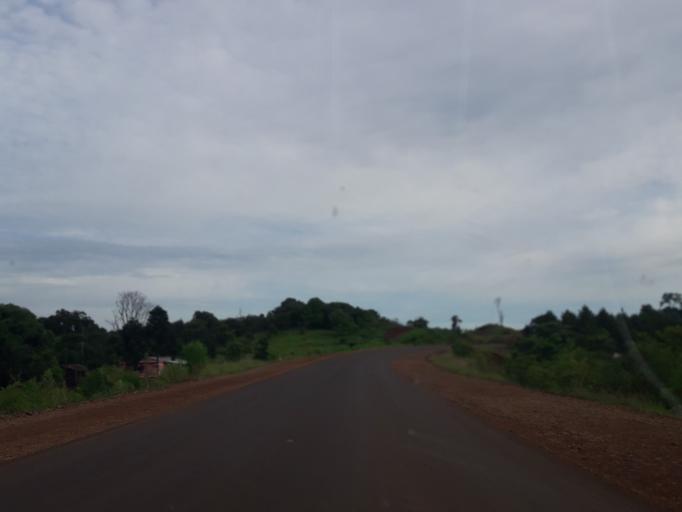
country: AR
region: Misiones
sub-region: Departamento de San Pedro
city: San Pedro
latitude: -26.5269
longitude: -53.9401
